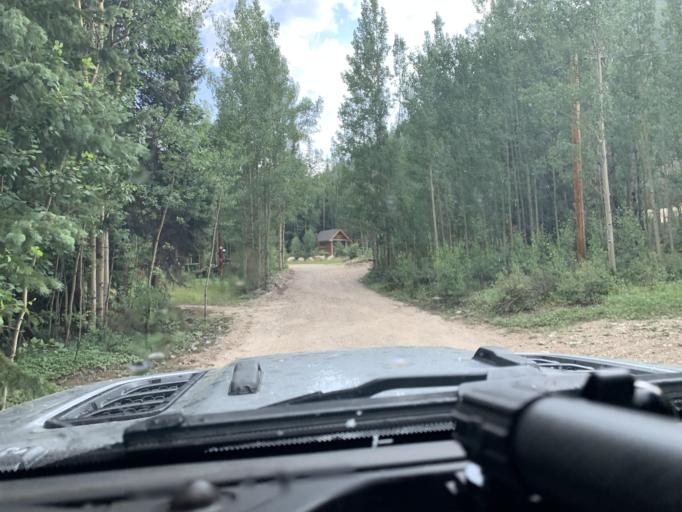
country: US
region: Colorado
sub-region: Chaffee County
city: Buena Vista
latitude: 38.6942
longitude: -106.3518
